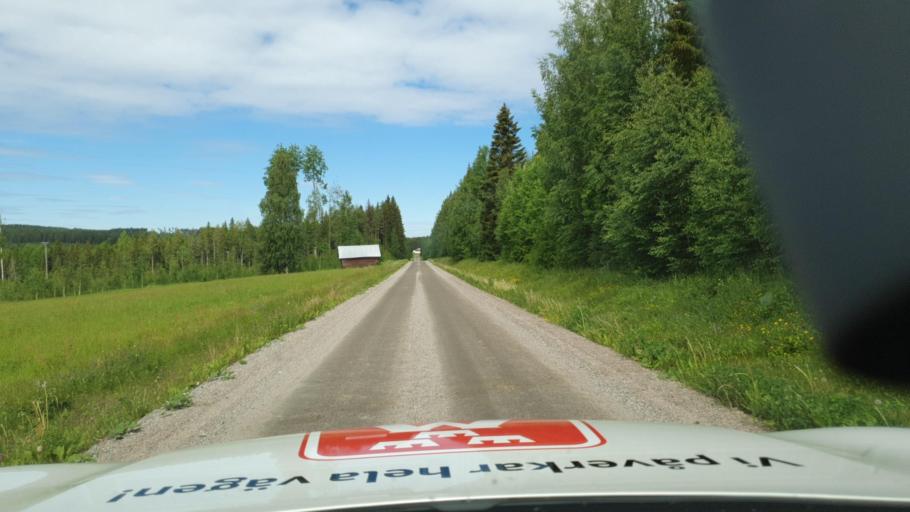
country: SE
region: Vaesterbotten
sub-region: Skelleftea Kommun
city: Burtraesk
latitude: 64.6285
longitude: 20.5541
